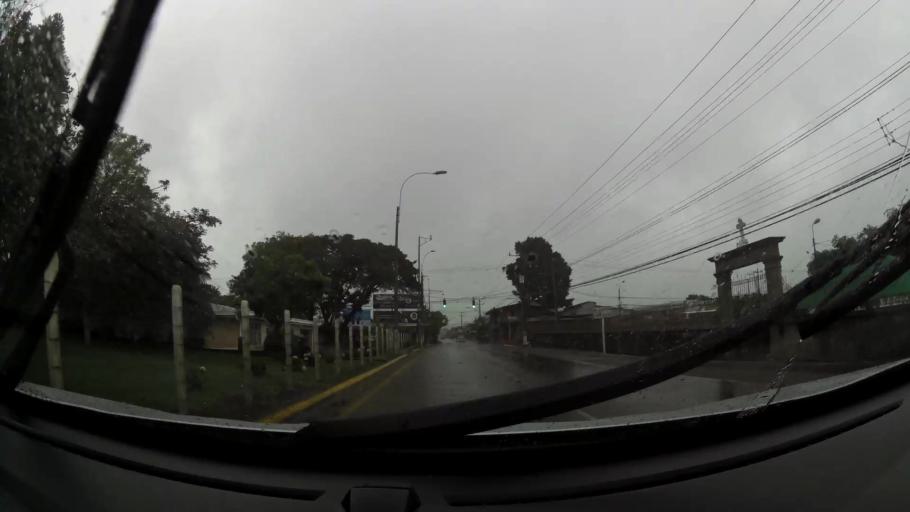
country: CR
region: Cartago
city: Cartago
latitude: 9.8665
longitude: -83.9329
